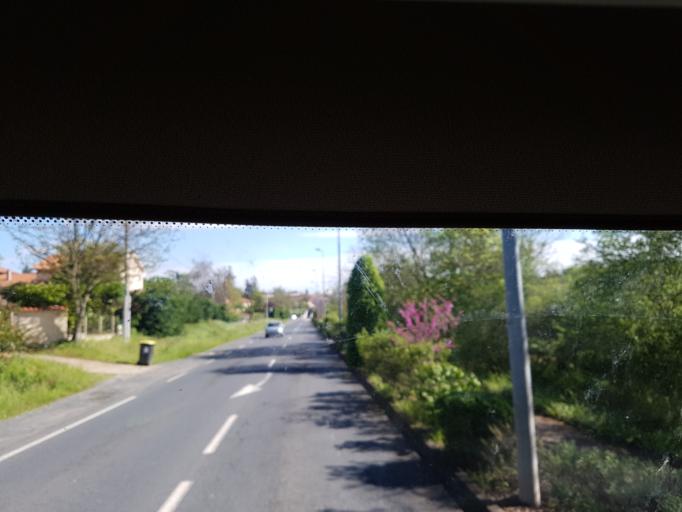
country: FR
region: Rhone-Alpes
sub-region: Departement du Rhone
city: Lentilly
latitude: 45.8186
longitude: 4.6660
